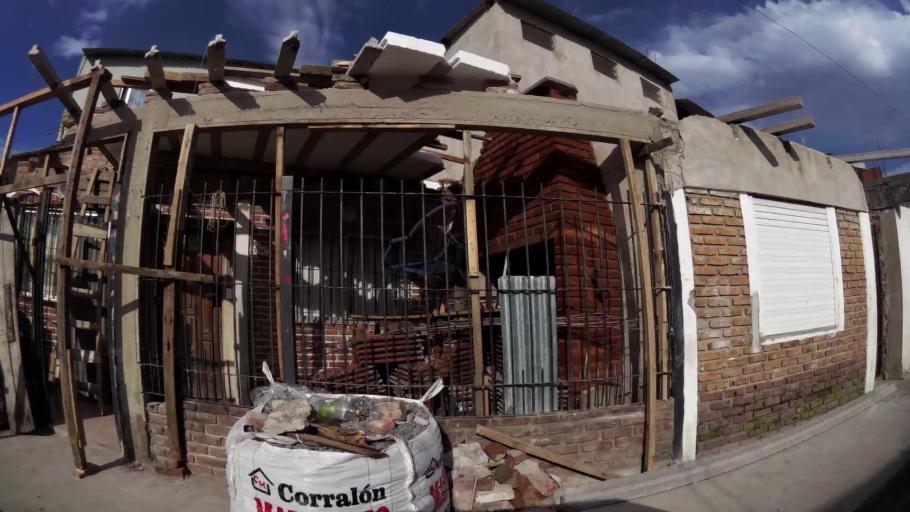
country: AR
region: Buenos Aires
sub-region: Partido de Lanus
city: Lanus
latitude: -34.7013
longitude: -58.3580
